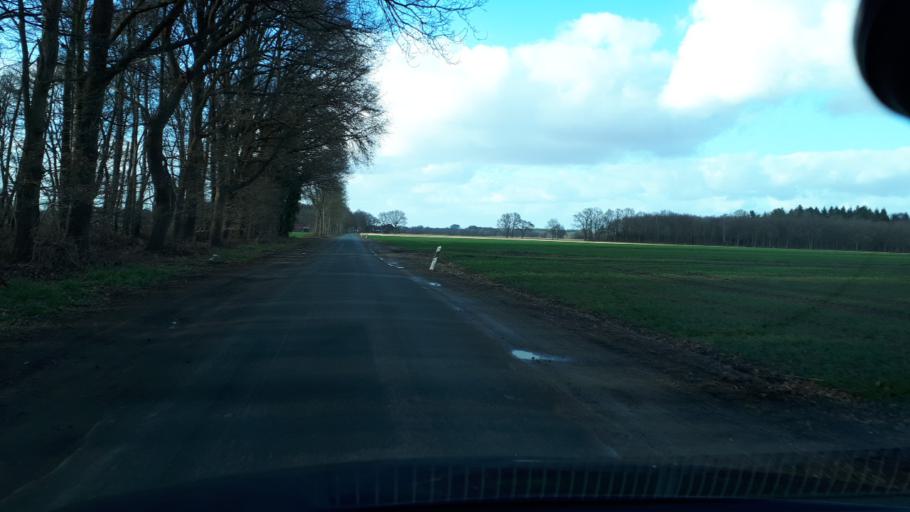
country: DE
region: Lower Saxony
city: Cloppenburg
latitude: 52.8384
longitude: 7.9976
